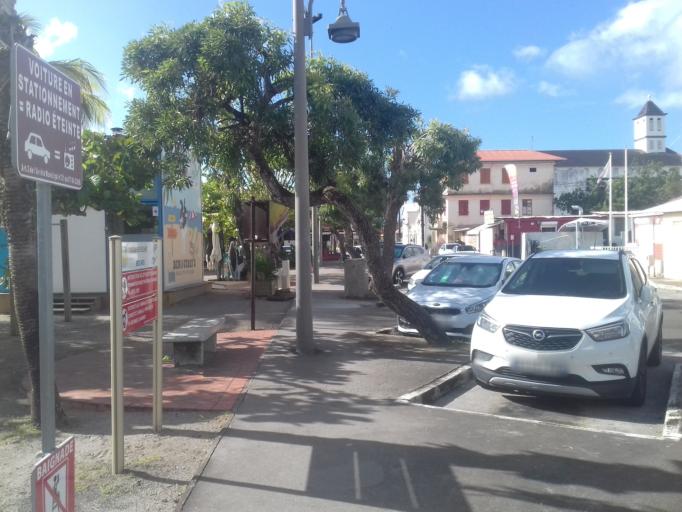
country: MQ
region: Martinique
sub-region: Martinique
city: Fort-de-France
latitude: 14.6153
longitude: -61.1011
